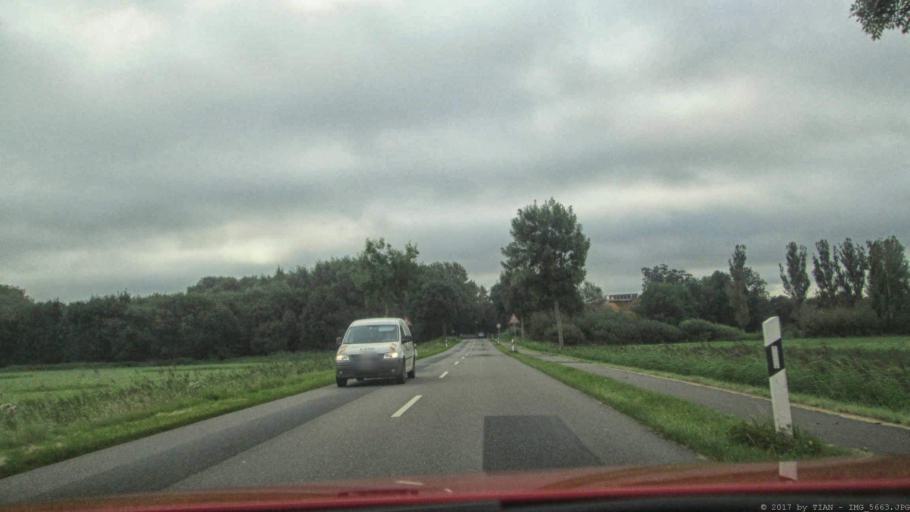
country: DE
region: Lower Saxony
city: Jembke
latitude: 52.4870
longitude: 10.7681
